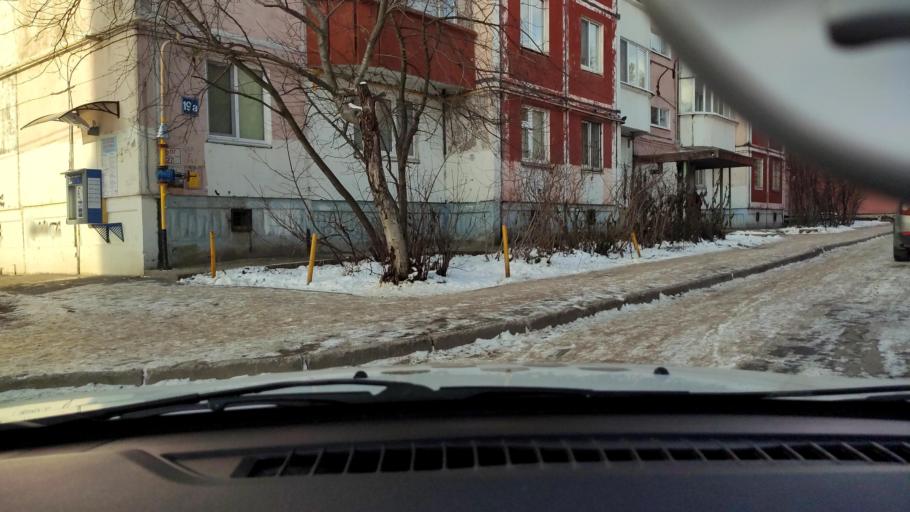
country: RU
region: Perm
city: Perm
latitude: 58.0880
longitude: 56.4124
